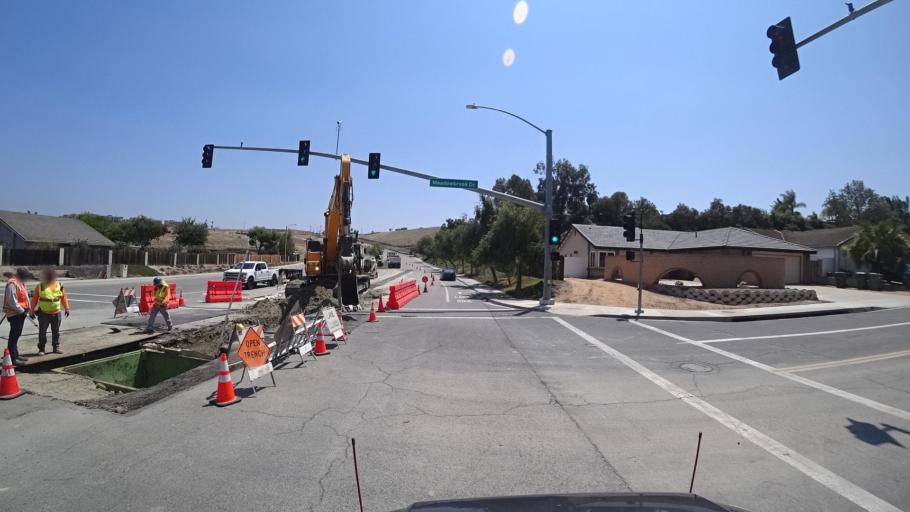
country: US
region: California
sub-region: San Diego County
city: Vista
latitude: 33.2235
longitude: -117.2632
